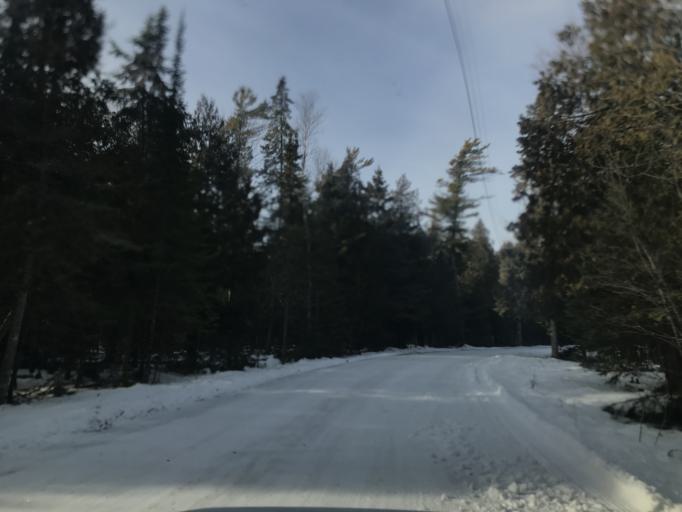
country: US
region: Wisconsin
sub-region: Door County
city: Sturgeon Bay
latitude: 45.1414
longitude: -87.0507
